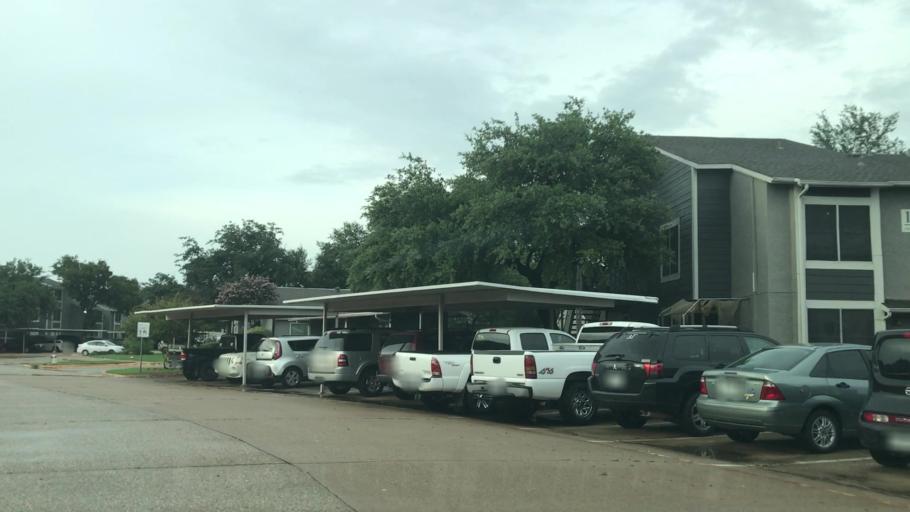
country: US
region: Texas
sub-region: Denton County
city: Lewisville
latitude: 33.0733
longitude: -97.0094
